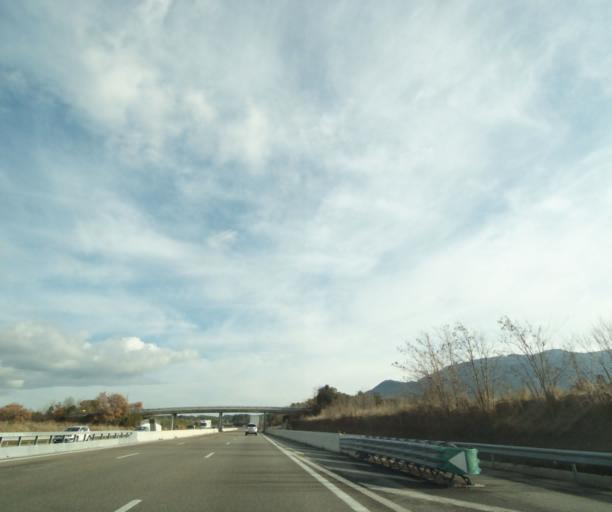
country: FR
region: Provence-Alpes-Cote d'Azur
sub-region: Departement du Var
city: Pourrieres
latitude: 43.4808
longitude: 5.7426
